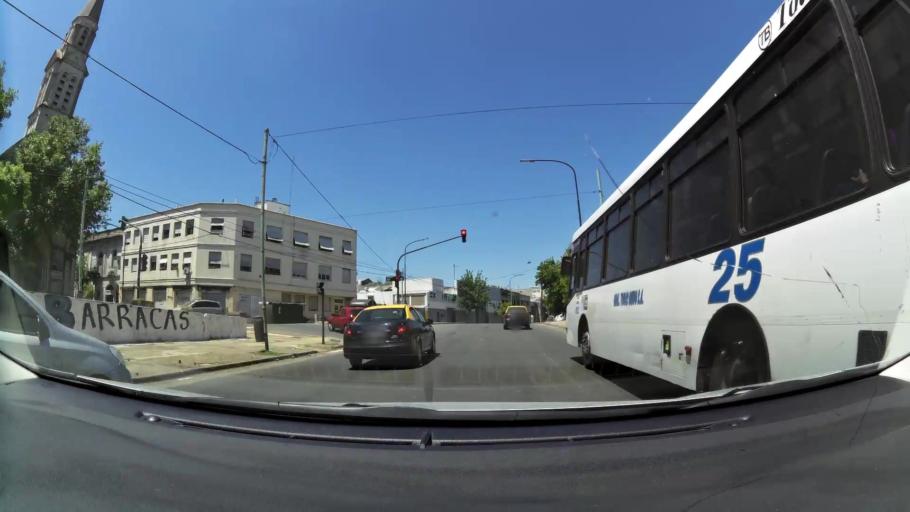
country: AR
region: Buenos Aires F.D.
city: Buenos Aires
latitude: -34.6341
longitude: -58.3828
